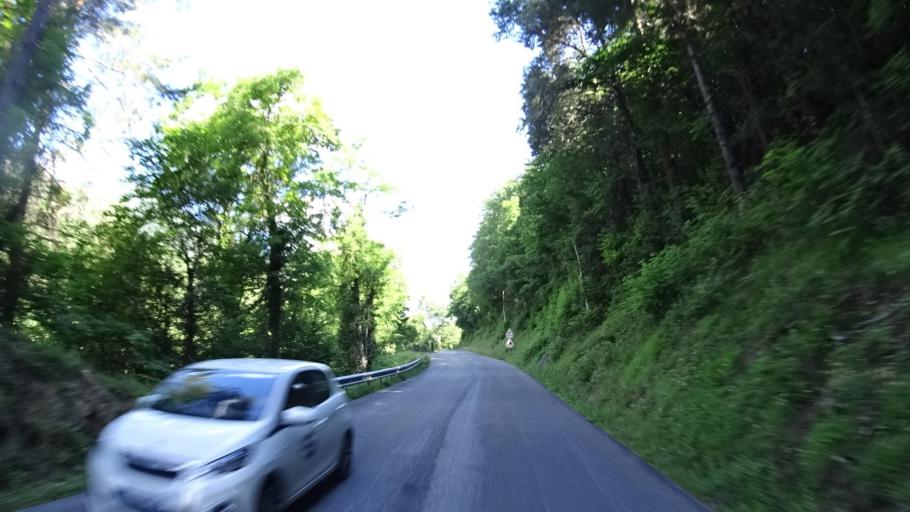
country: FR
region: Provence-Alpes-Cote d'Azur
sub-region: Departement des Alpes-de-Haute-Provence
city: Annot
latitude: 43.9761
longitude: 6.6532
